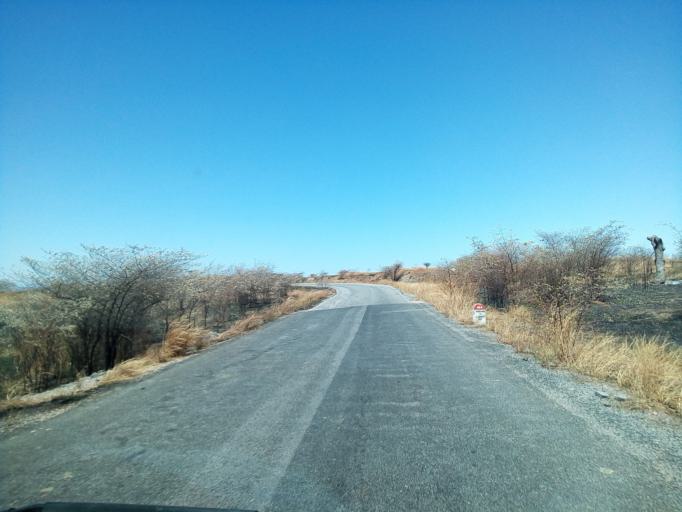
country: MG
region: Boeny
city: Ambato Boeny
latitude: -16.5745
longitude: 47.0938
